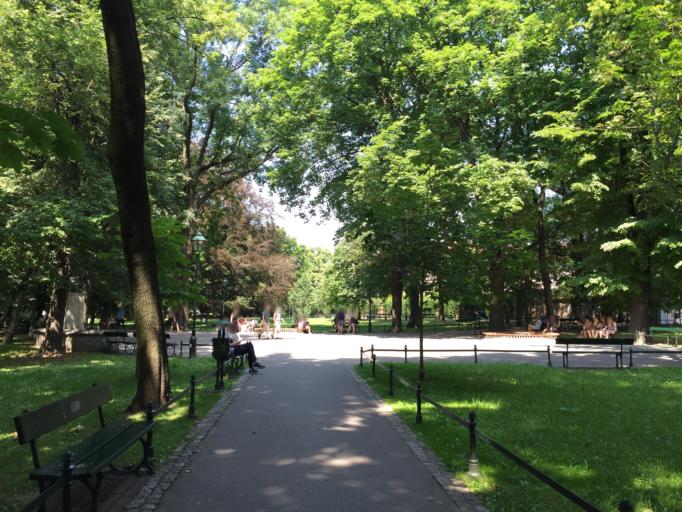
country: PL
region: Lesser Poland Voivodeship
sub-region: Krakow
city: Krakow
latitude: 50.0563
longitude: 19.9347
